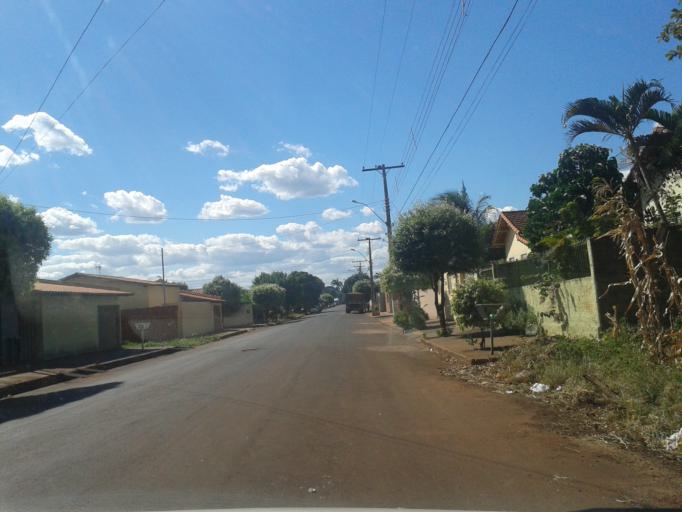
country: BR
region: Minas Gerais
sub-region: Capinopolis
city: Capinopolis
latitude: -18.6915
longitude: -49.5688
